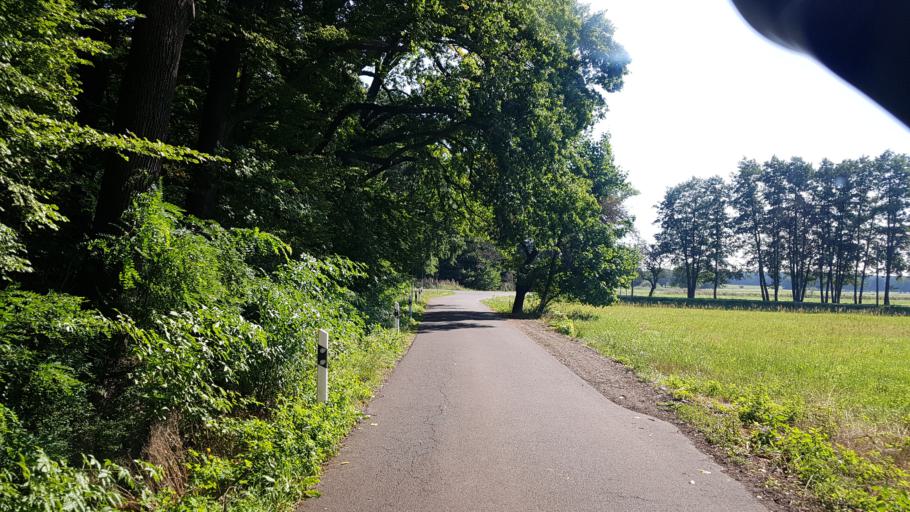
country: DE
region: Brandenburg
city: Vetschau
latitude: 51.7572
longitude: 14.0541
